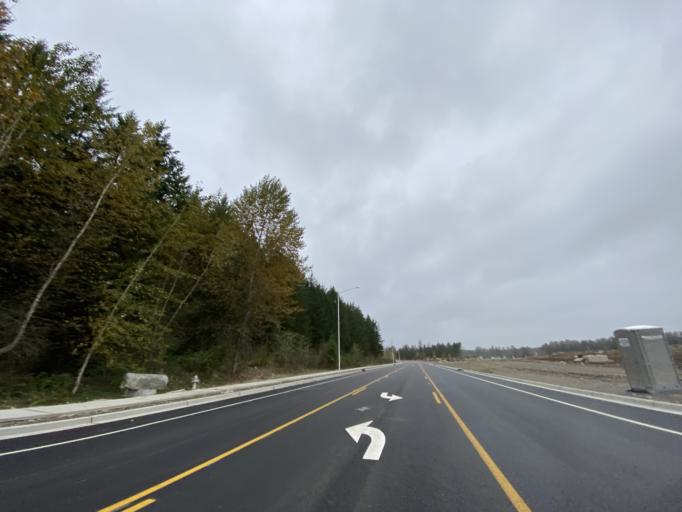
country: US
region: Washington
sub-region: Pierce County
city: South Hill
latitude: 47.0924
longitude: -122.2579
